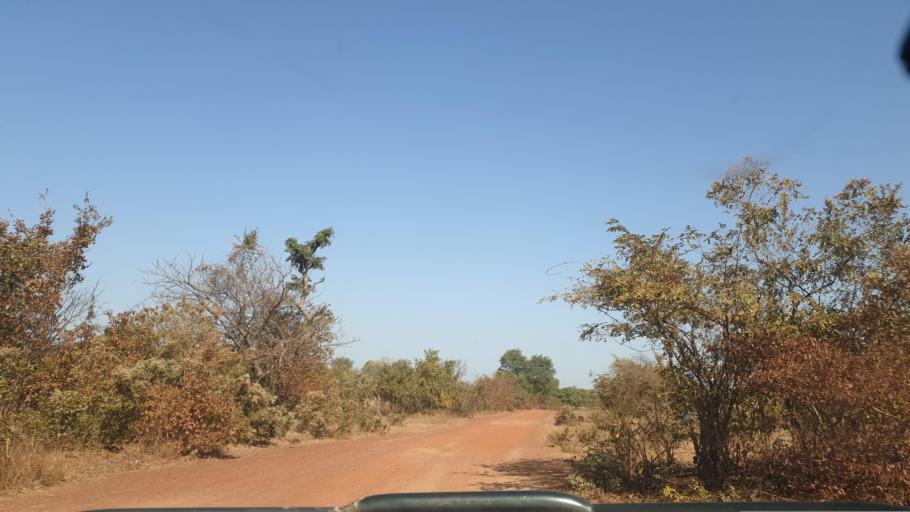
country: ML
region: Sikasso
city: Bougouni
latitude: 11.8321
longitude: -6.9787
